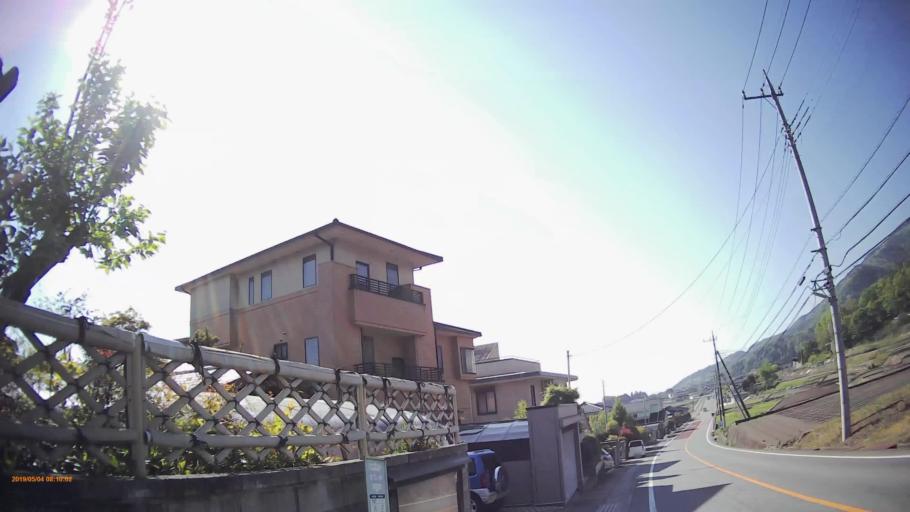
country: JP
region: Yamanashi
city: Nirasaki
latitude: 35.7393
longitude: 138.4078
